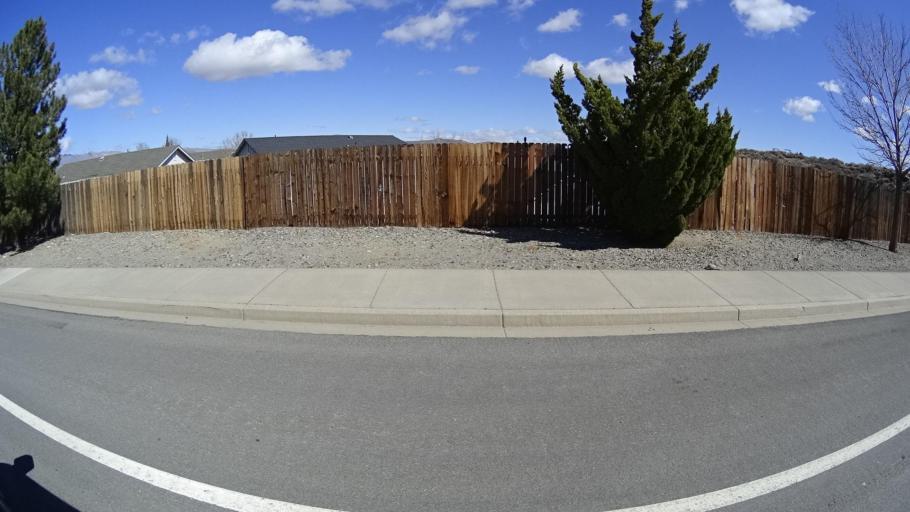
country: US
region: Nevada
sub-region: Washoe County
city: Lemmon Valley
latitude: 39.6252
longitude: -119.8978
